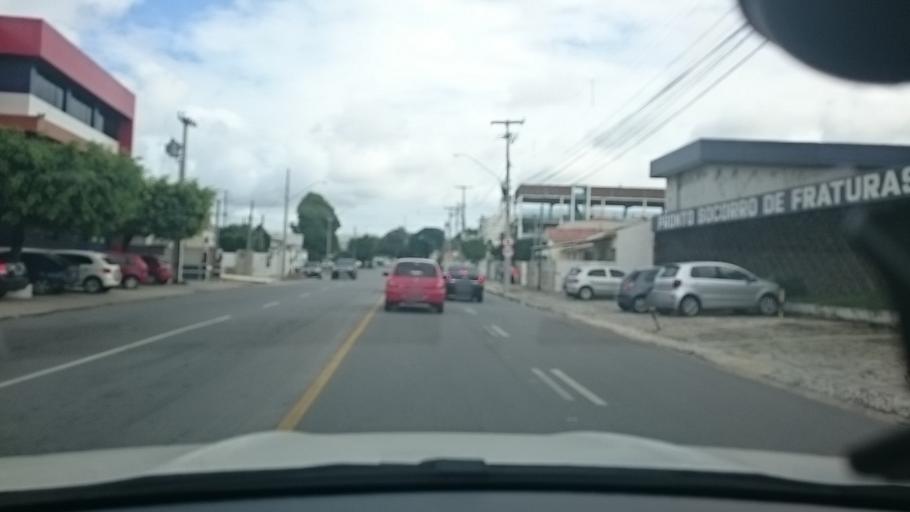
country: BR
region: Paraiba
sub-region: Joao Pessoa
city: Joao Pessoa
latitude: -7.1247
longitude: -34.8677
